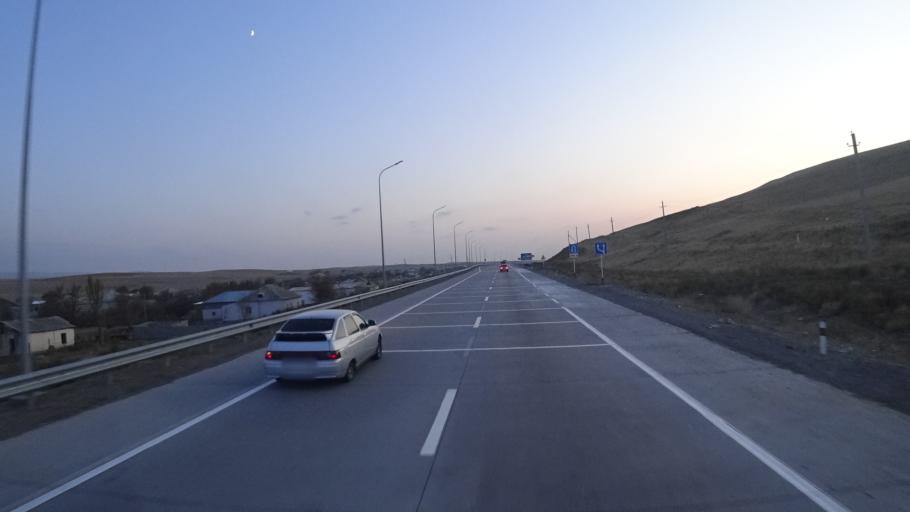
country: KZ
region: Ongtustik Qazaqstan
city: Qazyqurt
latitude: 41.8999
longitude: 69.4547
